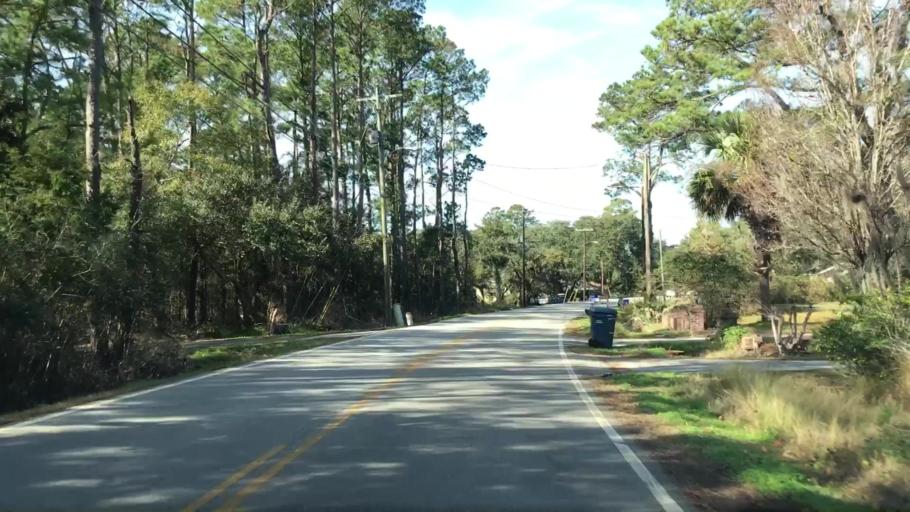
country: US
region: South Carolina
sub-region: Charleston County
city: Charleston
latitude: 32.7749
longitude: -80.0165
